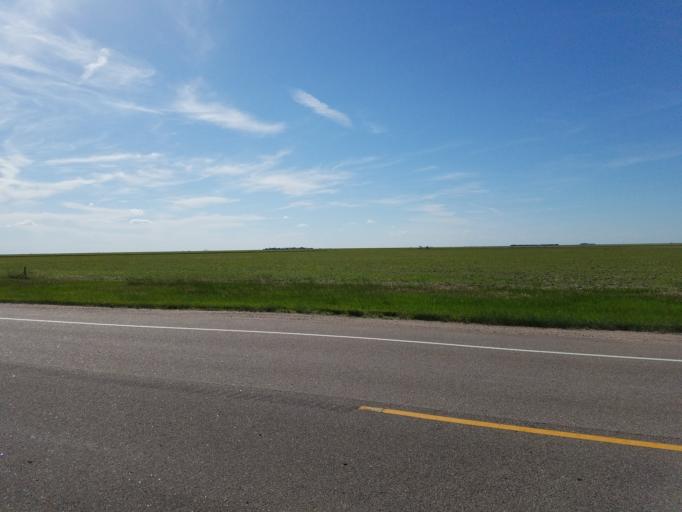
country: US
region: Kansas
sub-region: Cheyenne County
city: Saint Francis
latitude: 39.7512
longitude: -102.0506
